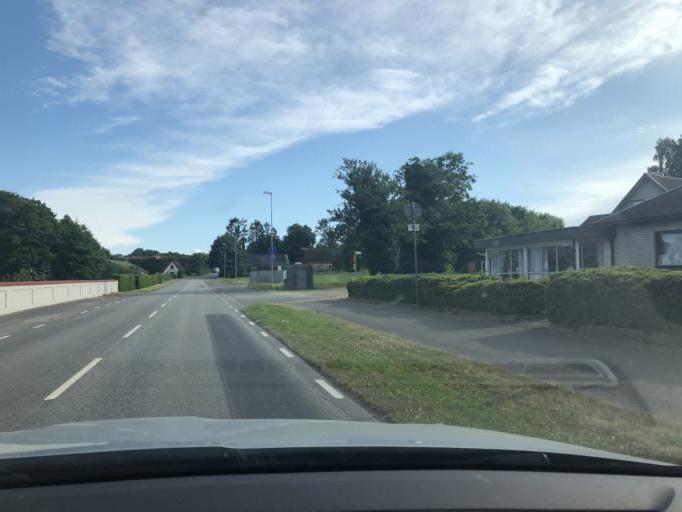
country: SE
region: Blekinge
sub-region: Solvesborgs Kommun
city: Soelvesborg
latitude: 56.0600
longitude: 14.5356
